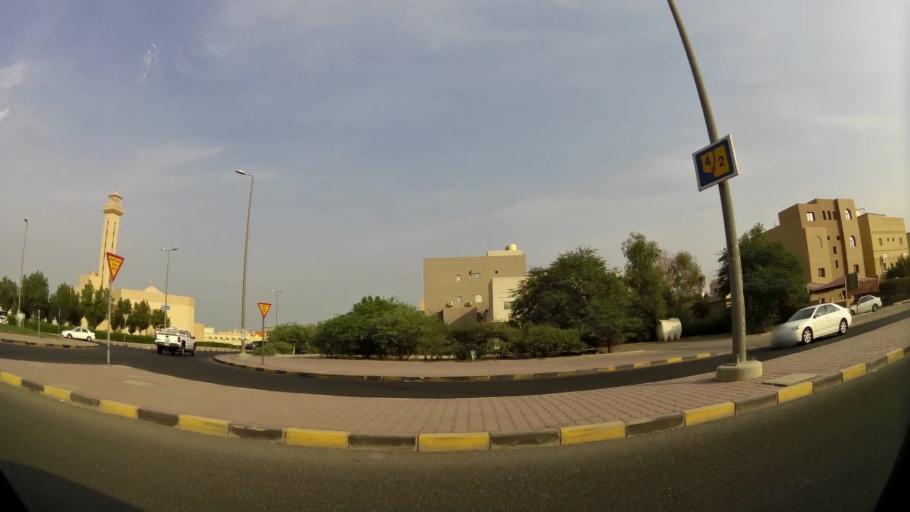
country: KW
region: Mubarak al Kabir
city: Sabah as Salim
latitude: 29.2307
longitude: 48.0612
